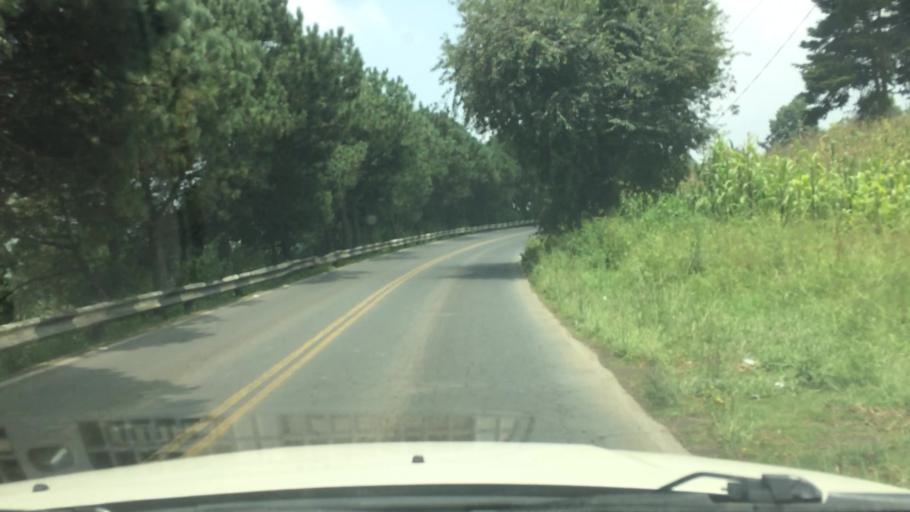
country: MX
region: Mexico City
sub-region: Tlalpan
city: Lomas de Tepemecatl
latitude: 19.2315
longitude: -99.2165
